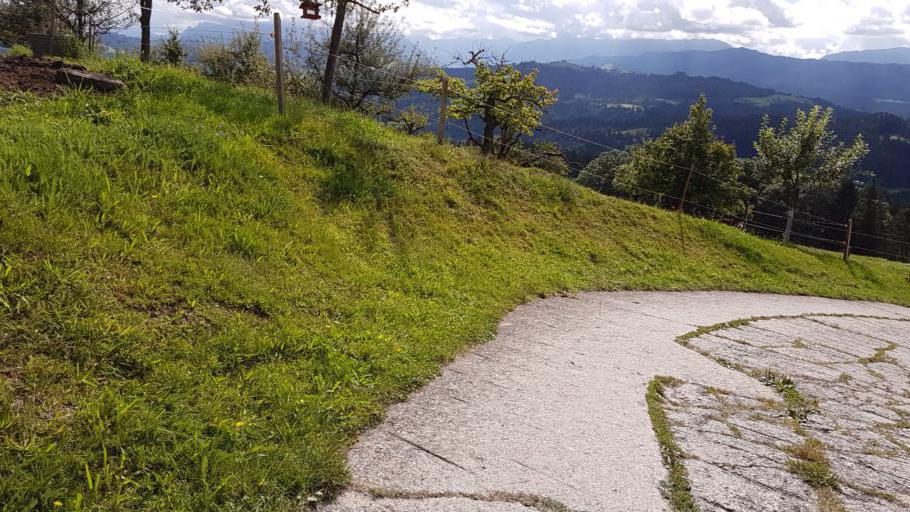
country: CH
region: Bern
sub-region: Bern-Mittelland District
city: Bowil
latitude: 46.8636
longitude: 7.7074
